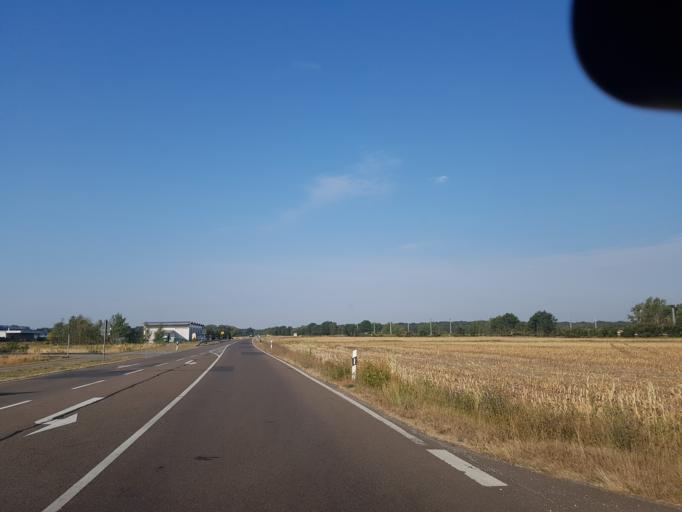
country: DE
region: Saxony
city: Nauwalde
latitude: 51.4051
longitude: 13.4345
